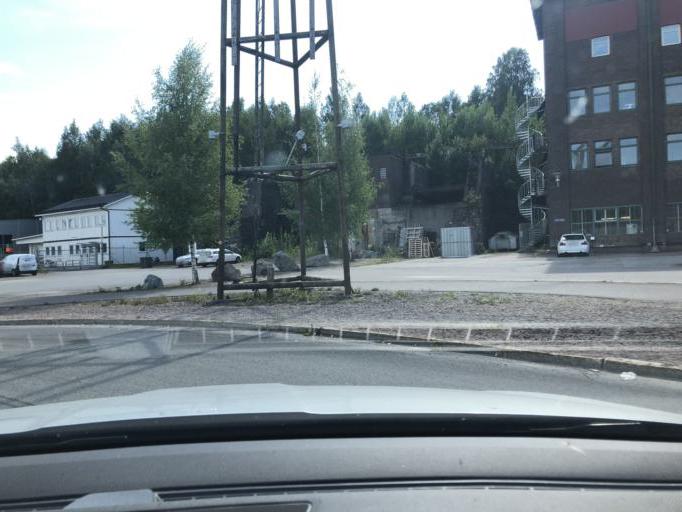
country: SE
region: Dalarna
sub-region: Avesta Kommun
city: Avesta
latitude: 60.1479
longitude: 16.1750
